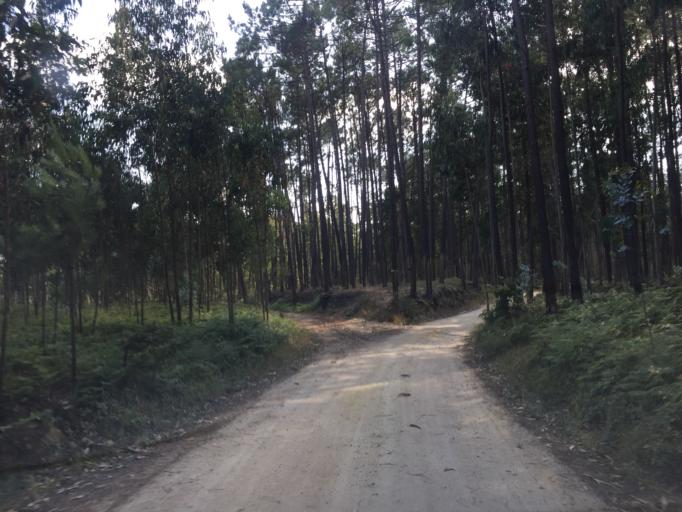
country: PT
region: Leiria
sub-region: Leiria
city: Monte Redondo
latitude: 39.9645
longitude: -8.8021
